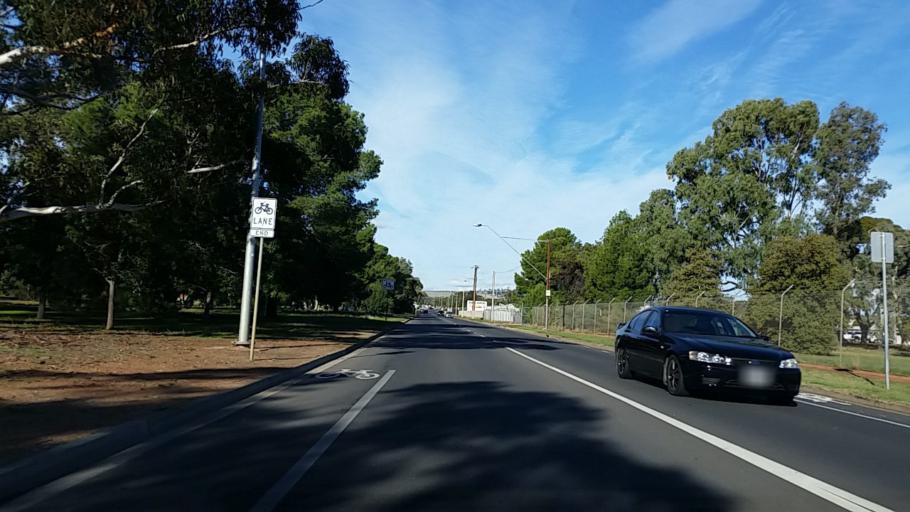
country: AU
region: South Australia
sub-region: Salisbury
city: Elizabeth
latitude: -34.6989
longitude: 138.6593
